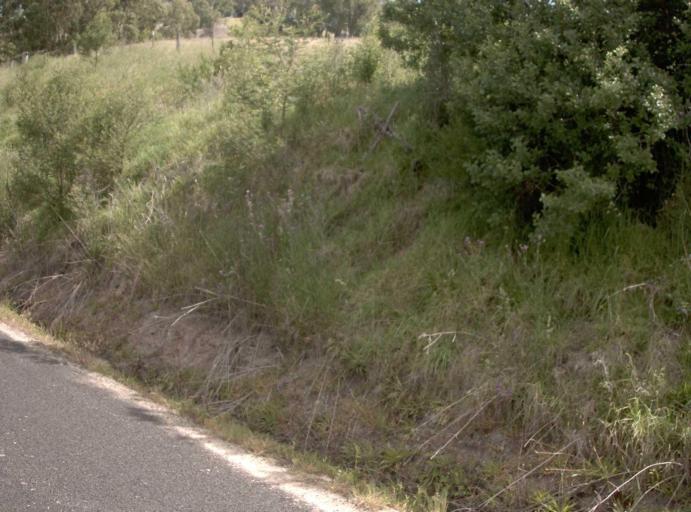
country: AU
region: New South Wales
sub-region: Bega Valley
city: Eden
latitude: -37.4767
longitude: 149.5958
